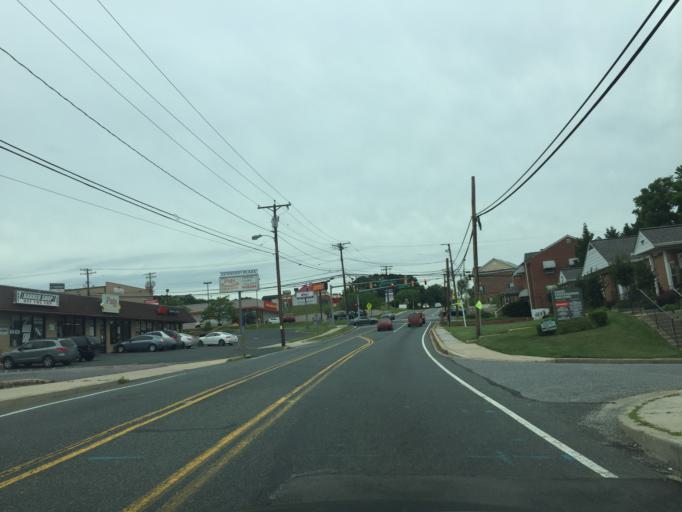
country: US
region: Maryland
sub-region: Baltimore County
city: Rosedale
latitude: 39.3397
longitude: -76.5053
